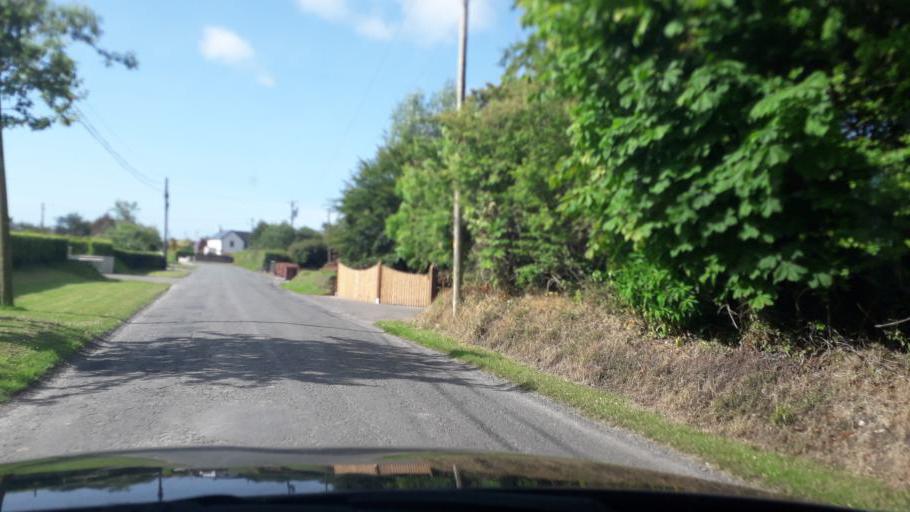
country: IE
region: Leinster
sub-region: Loch Garman
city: Loch Garman
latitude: 52.2453
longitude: -6.5504
